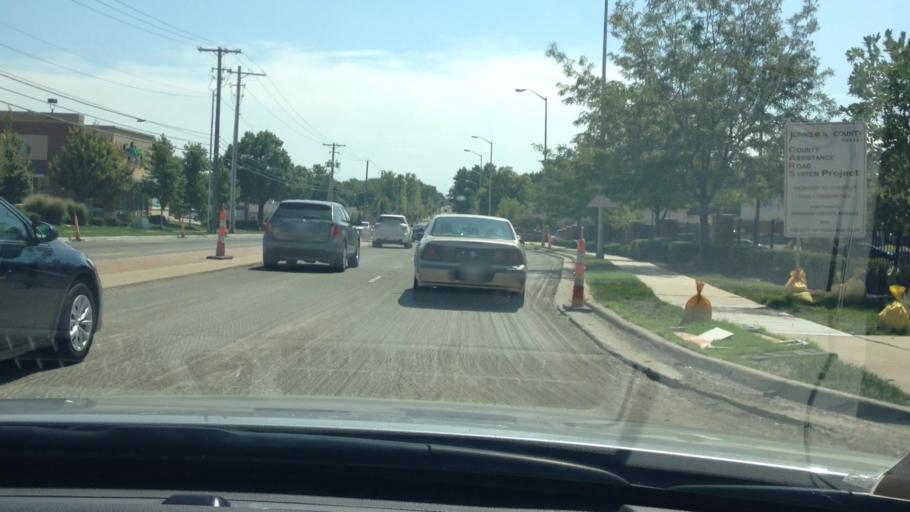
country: US
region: Kansas
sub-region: Johnson County
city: Overland Park
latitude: 38.9566
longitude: -94.6864
